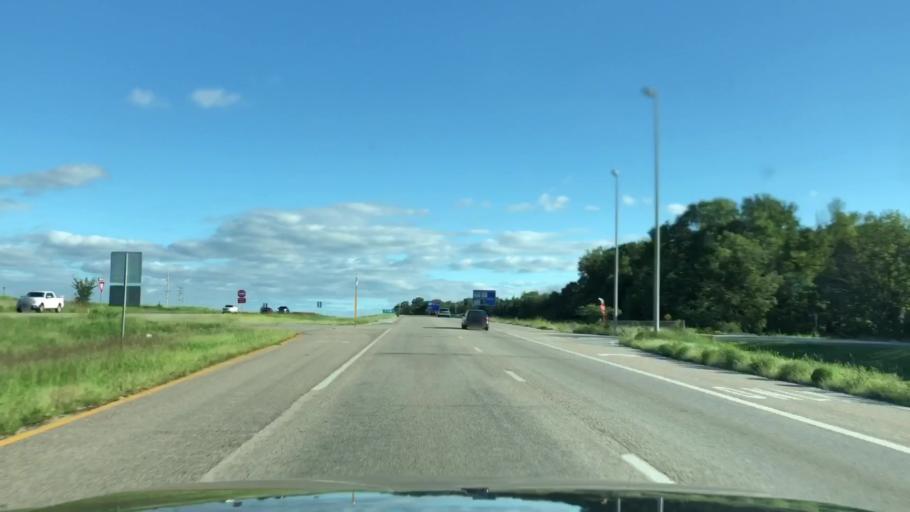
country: US
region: Missouri
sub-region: Saint Charles County
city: Wentzville
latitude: 38.8323
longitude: -90.8556
